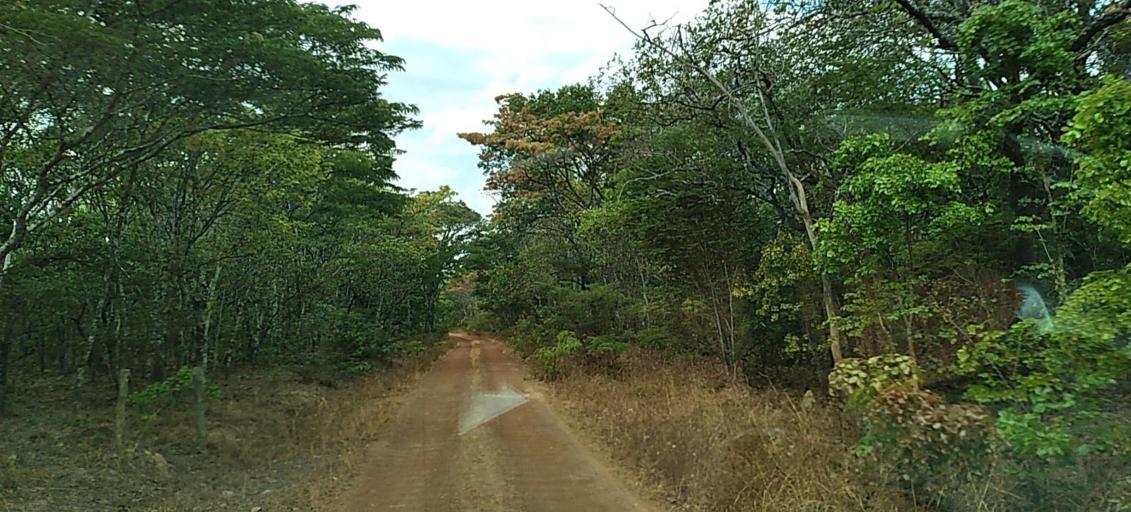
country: ZM
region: Copperbelt
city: Chililabombwe
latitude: -12.4514
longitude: 27.6119
